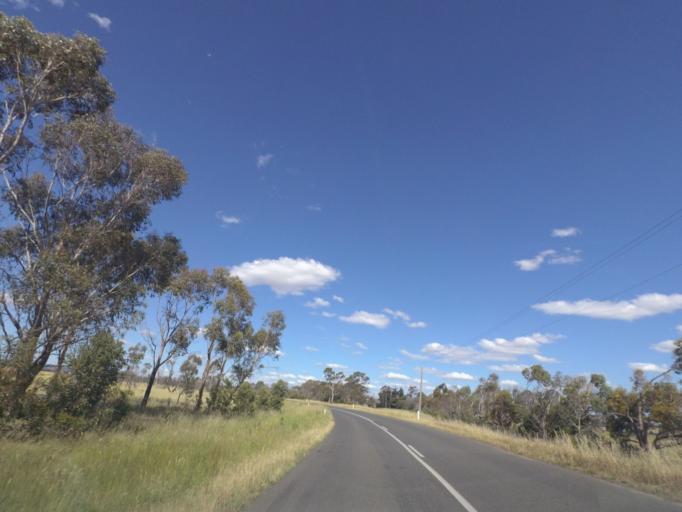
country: AU
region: Victoria
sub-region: Hume
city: Craigieburn
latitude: -37.4275
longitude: 144.8708
